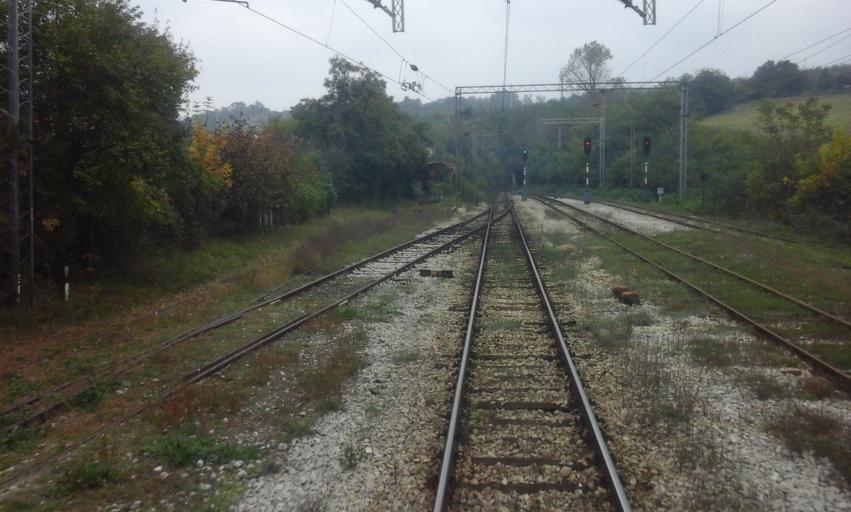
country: RS
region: Central Serbia
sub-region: Belgrade
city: Sopot
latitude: 44.5676
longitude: 20.5635
